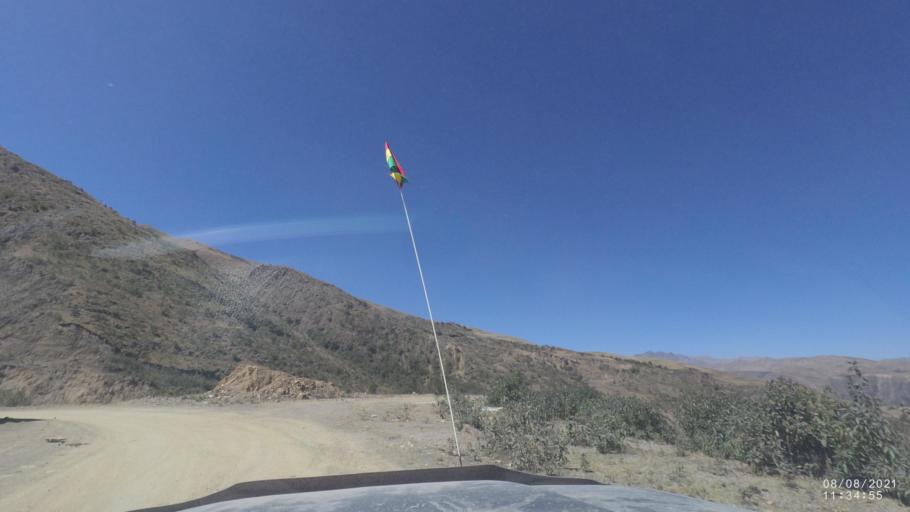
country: BO
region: Cochabamba
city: Colchani
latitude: -16.7774
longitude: -66.6451
